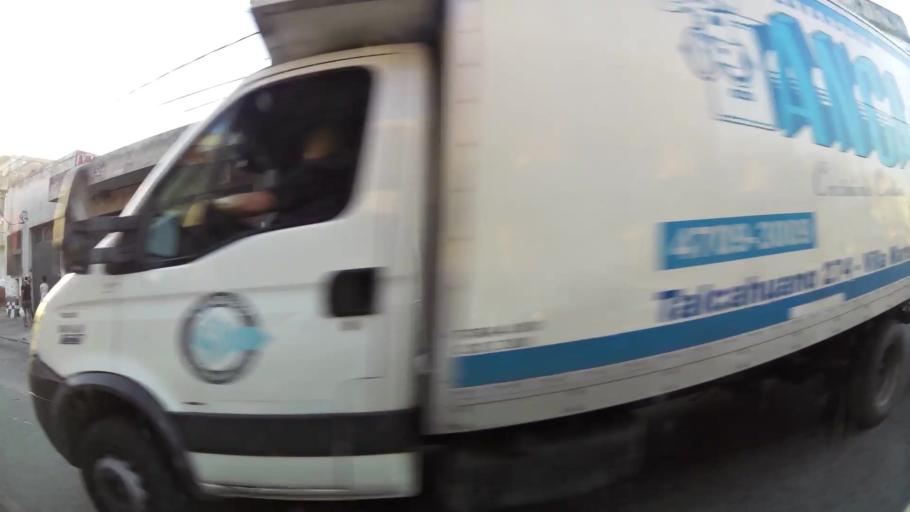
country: AR
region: Buenos Aires
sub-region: Partido de General San Martin
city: General San Martin
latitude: -34.5521
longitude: -58.5133
